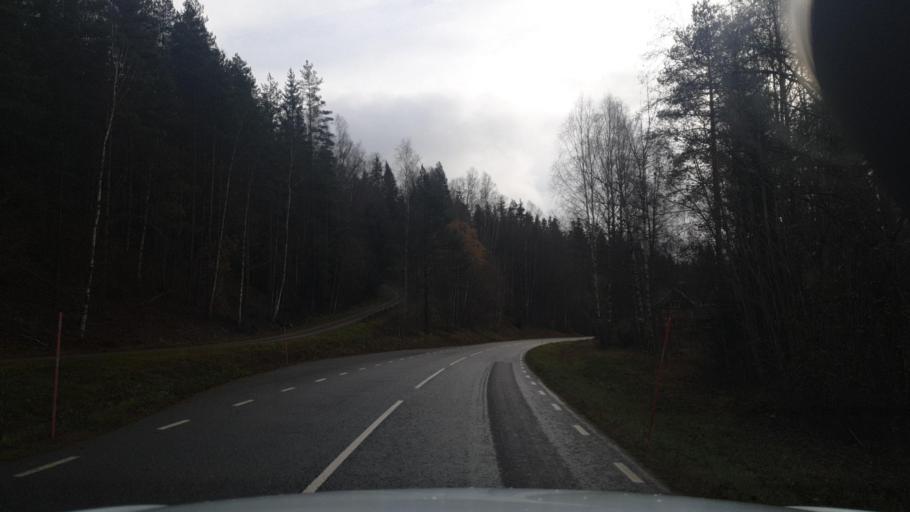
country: NO
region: Ostfold
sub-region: Romskog
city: Romskog
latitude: 59.6973
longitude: 12.0883
